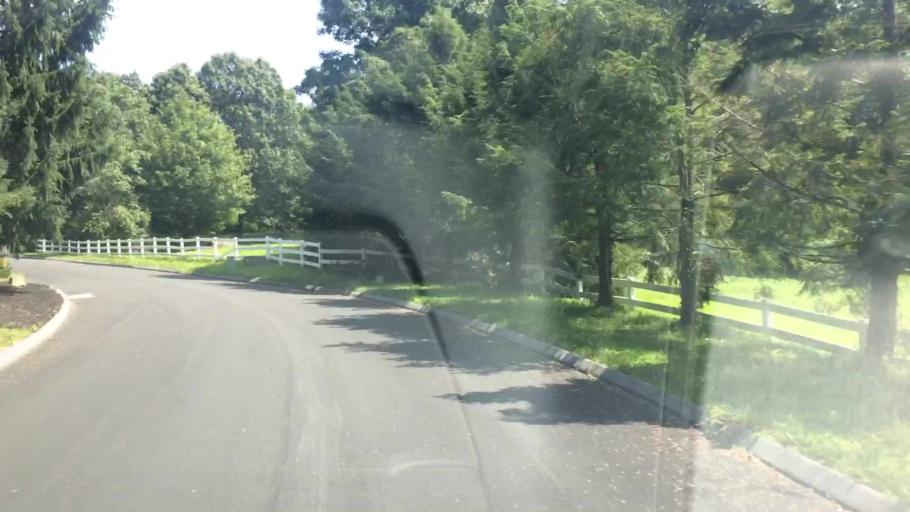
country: US
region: Connecticut
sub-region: Fairfield County
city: Danbury
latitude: 41.4127
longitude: -73.5041
